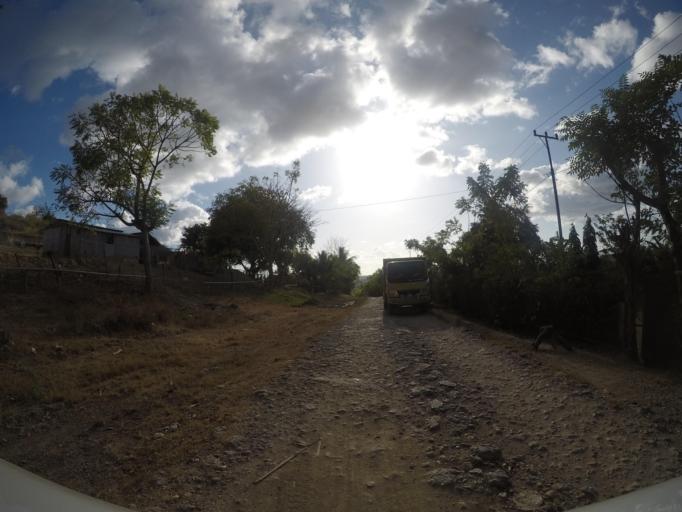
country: TL
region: Lautem
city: Lospalos
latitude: -8.4296
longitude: 126.8461
